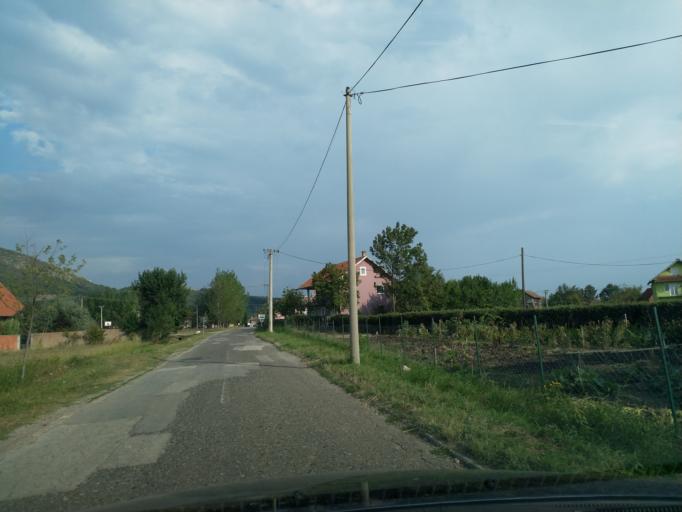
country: RS
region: Central Serbia
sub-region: Pomoravski Okrug
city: Paracin
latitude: 43.8223
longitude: 21.5377
